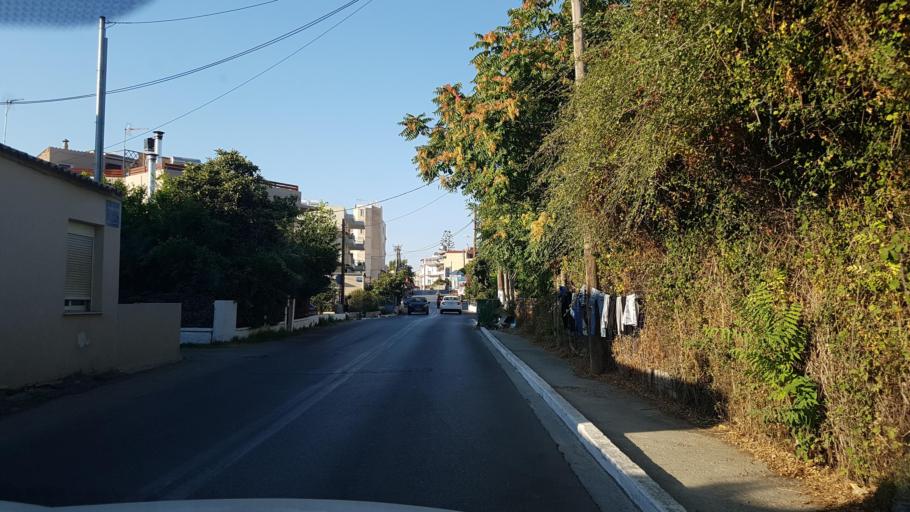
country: GR
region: Crete
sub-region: Nomos Chanias
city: Chania
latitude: 35.5061
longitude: 24.0084
